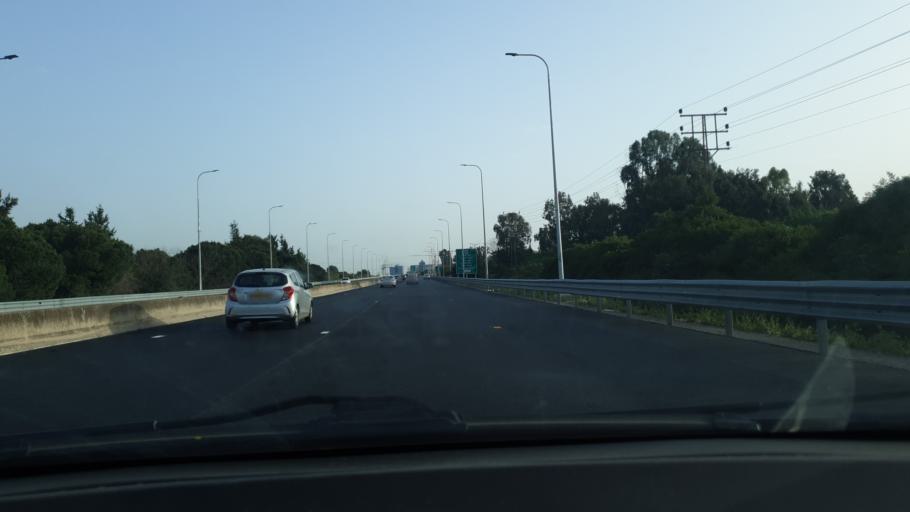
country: IL
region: Central District
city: Ra'anana
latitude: 32.2145
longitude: 34.8835
